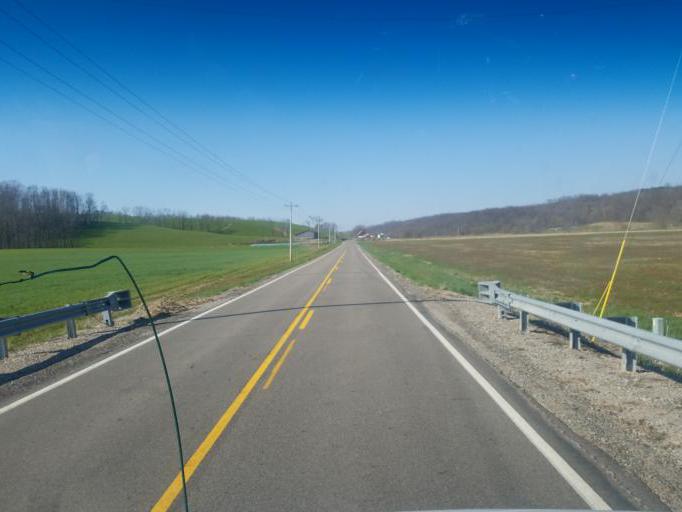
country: US
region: Ohio
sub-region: Muskingum County
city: Frazeysburg
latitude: 40.2890
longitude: -82.0896
